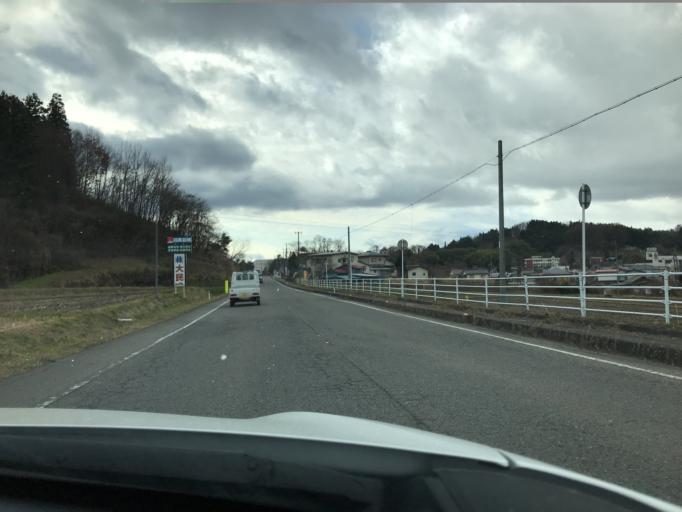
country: JP
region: Fukushima
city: Nihommatsu
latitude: 37.6030
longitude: 140.5819
